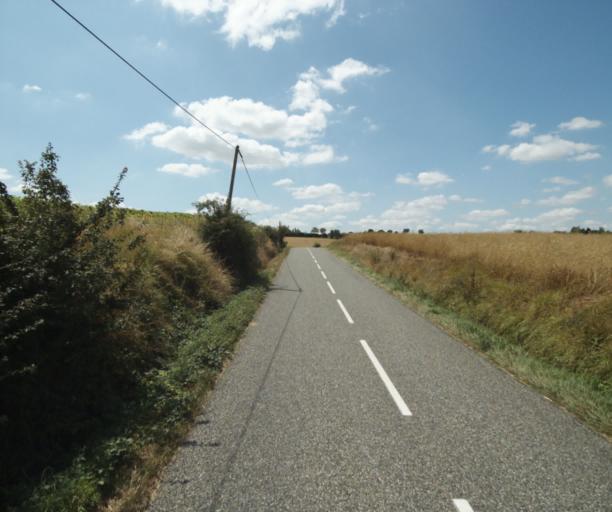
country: FR
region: Midi-Pyrenees
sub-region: Departement de la Haute-Garonne
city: Saint-Felix-Lauragais
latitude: 43.4657
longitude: 1.8341
